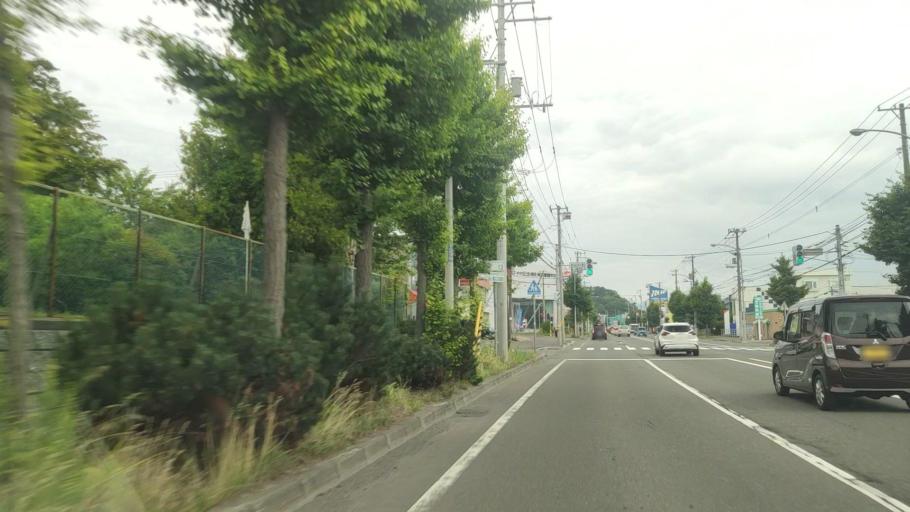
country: JP
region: Hokkaido
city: Sapporo
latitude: 42.9614
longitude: 141.3170
